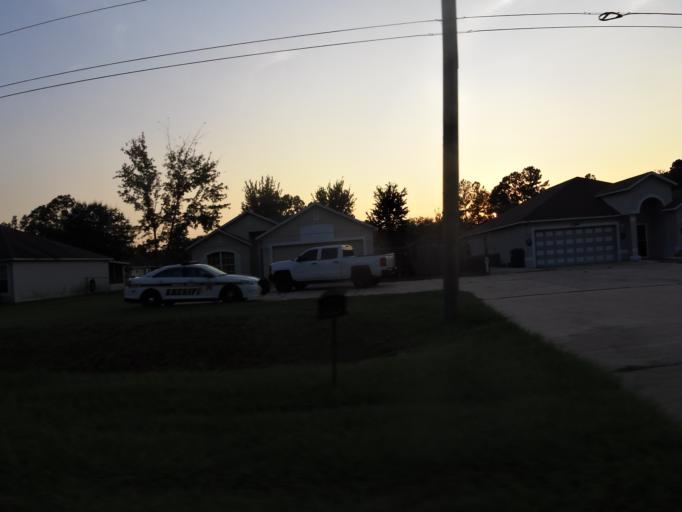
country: US
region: Florida
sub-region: Baker County
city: Macclenny
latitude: 30.2915
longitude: -82.1243
